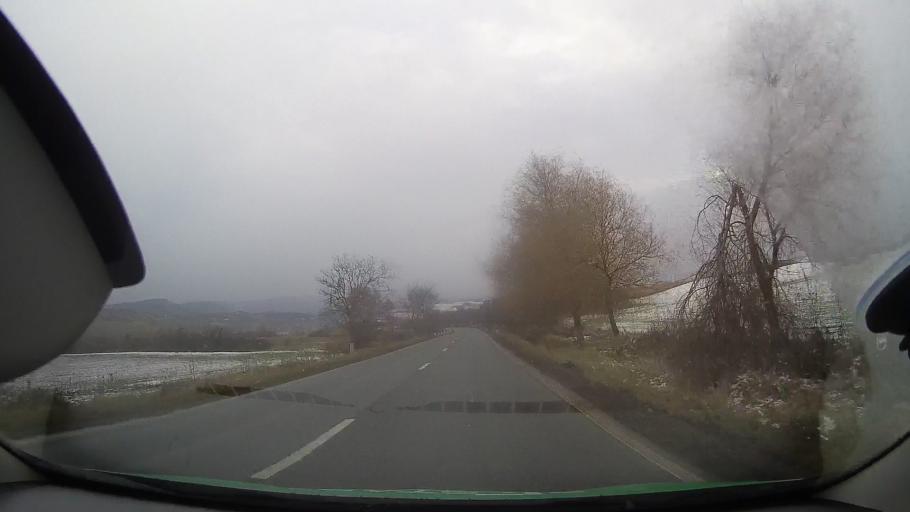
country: RO
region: Sibiu
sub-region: Comuna Blajel
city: Blajel
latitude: 46.2471
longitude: 24.3002
